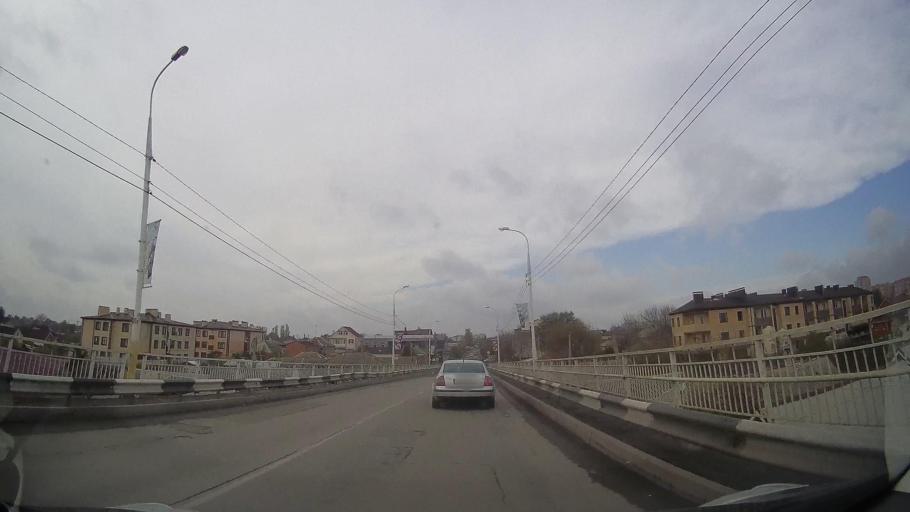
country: RU
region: Rostov
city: Bataysk
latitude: 47.1516
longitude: 39.7546
